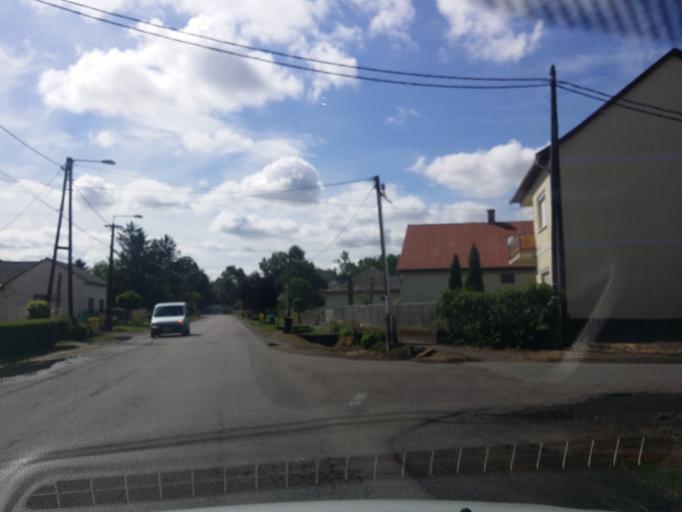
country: HU
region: Jasz-Nagykun-Szolnok
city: Jaszszentandras
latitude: 47.6486
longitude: 20.1585
